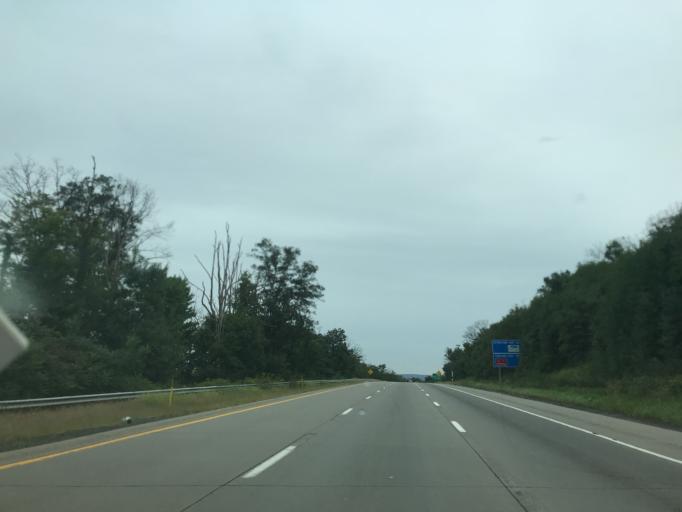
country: US
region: Pennsylvania
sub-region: Luzerne County
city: Harleigh
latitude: 41.0657
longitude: -75.9867
